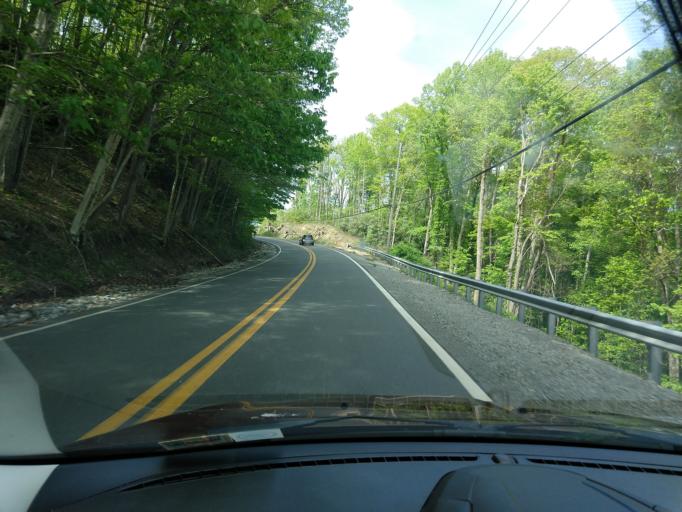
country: US
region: West Virginia
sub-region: Raleigh County
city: Daniels
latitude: 37.7822
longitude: -81.1136
